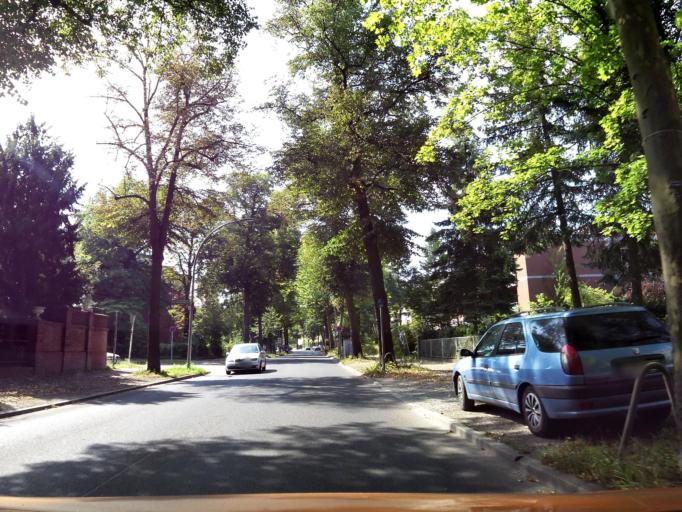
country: DE
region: Berlin
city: Lichterfelde
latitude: 52.4329
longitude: 13.3188
